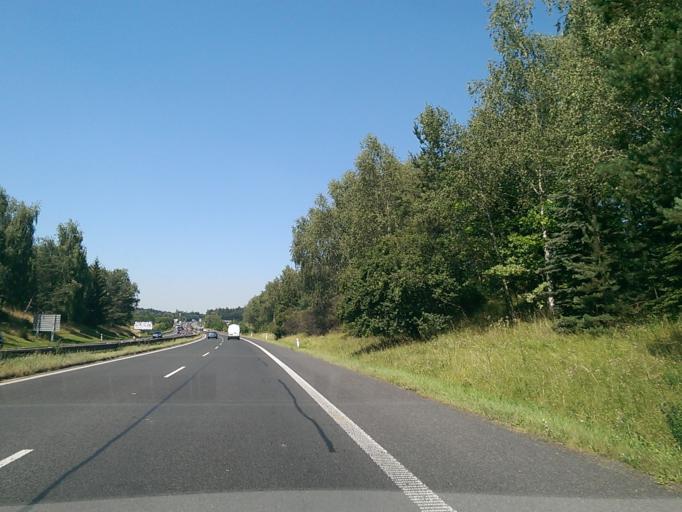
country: CZ
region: Central Bohemia
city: Lustenice
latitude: 50.3323
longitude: 14.8761
